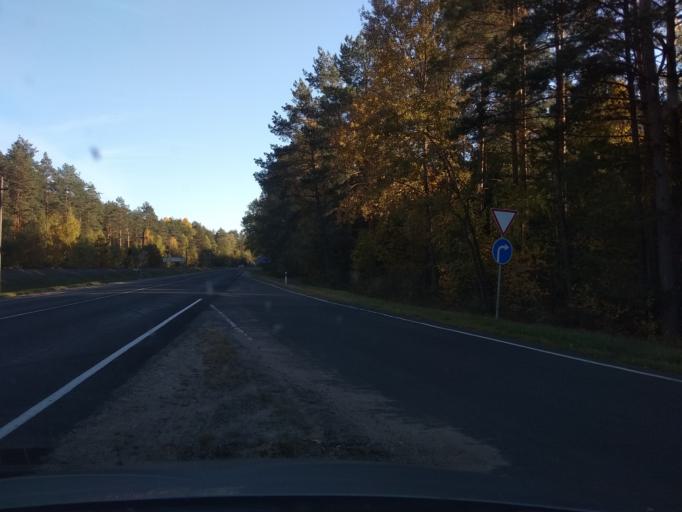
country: BY
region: Brest
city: Nyakhachava
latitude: 52.5719
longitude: 25.1165
